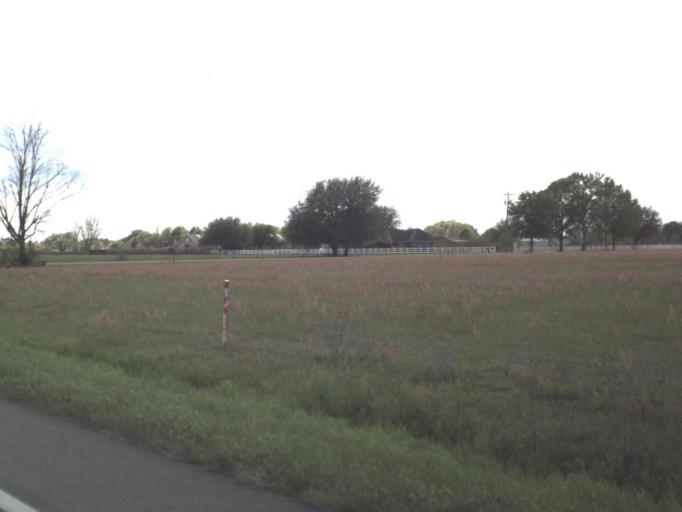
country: US
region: Florida
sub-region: Okaloosa County
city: Crestview
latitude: 30.8533
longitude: -86.5282
